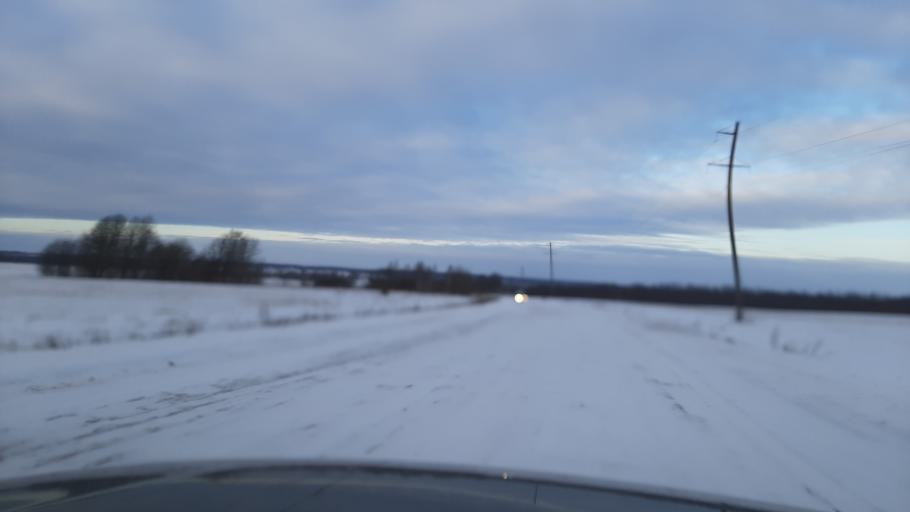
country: RU
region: Kostroma
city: Kosmynino
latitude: 57.4831
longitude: 40.8366
